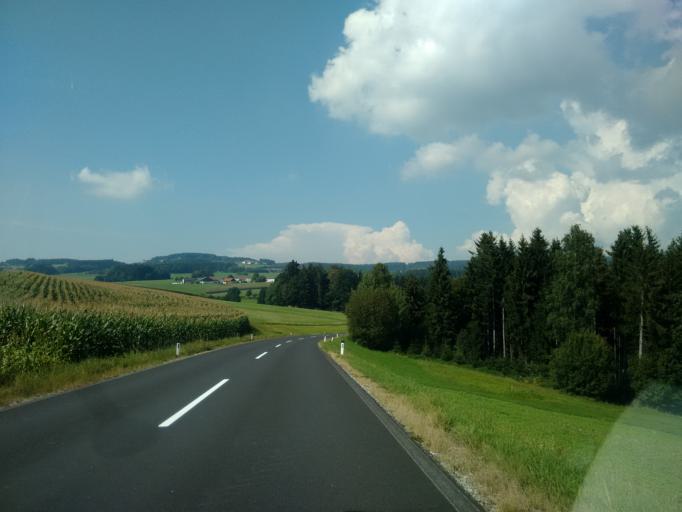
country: AT
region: Upper Austria
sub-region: Politischer Bezirk Urfahr-Umgebung
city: Altenberg bei Linz
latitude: 48.3975
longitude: 14.3452
